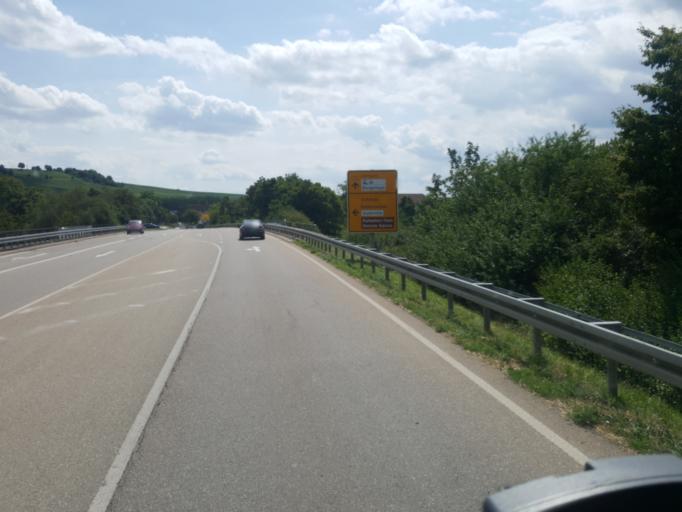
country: DE
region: Baden-Wuerttemberg
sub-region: Freiburg Region
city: Mullheim
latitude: 47.8159
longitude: 7.6117
